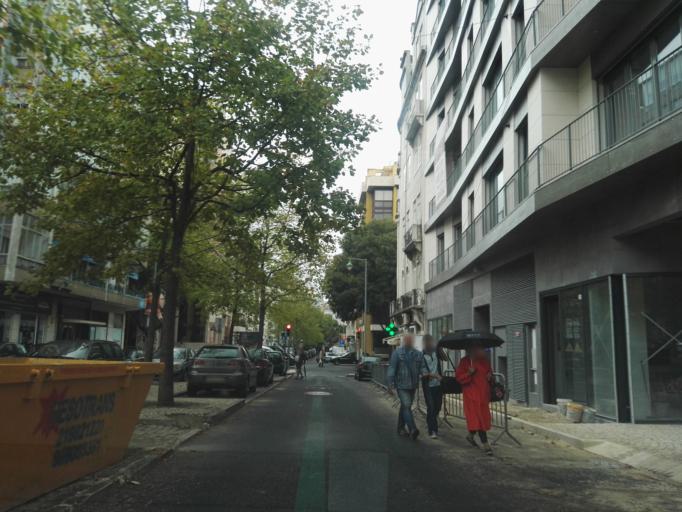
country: PT
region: Lisbon
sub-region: Lisbon
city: Lisbon
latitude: 38.7379
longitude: -9.1490
